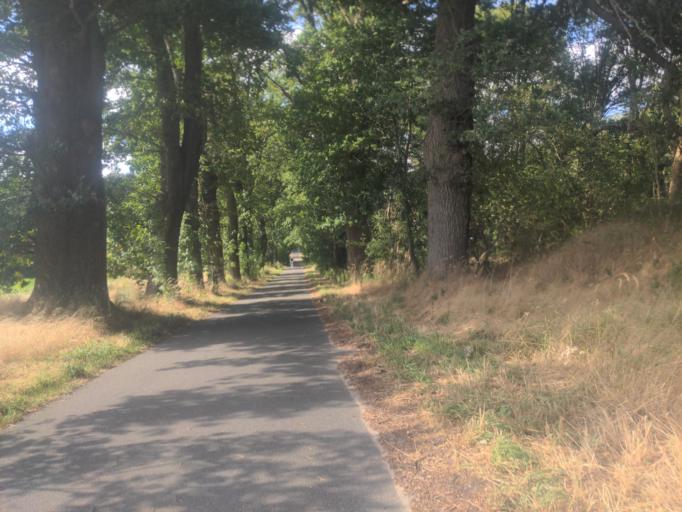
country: DE
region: Lower Saxony
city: Neu Darchau
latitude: 53.2059
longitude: 10.8636
